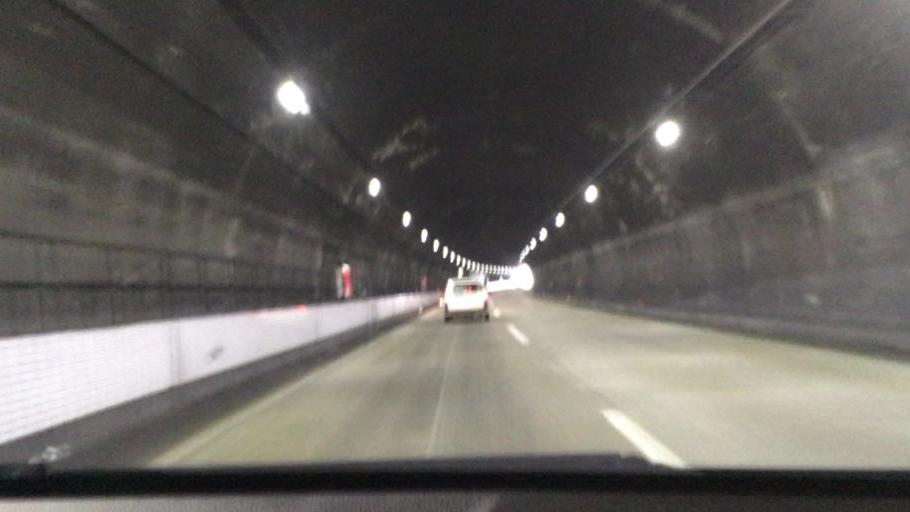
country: JP
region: Yamaguchi
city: Tokuyama
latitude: 34.0700
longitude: 131.7080
